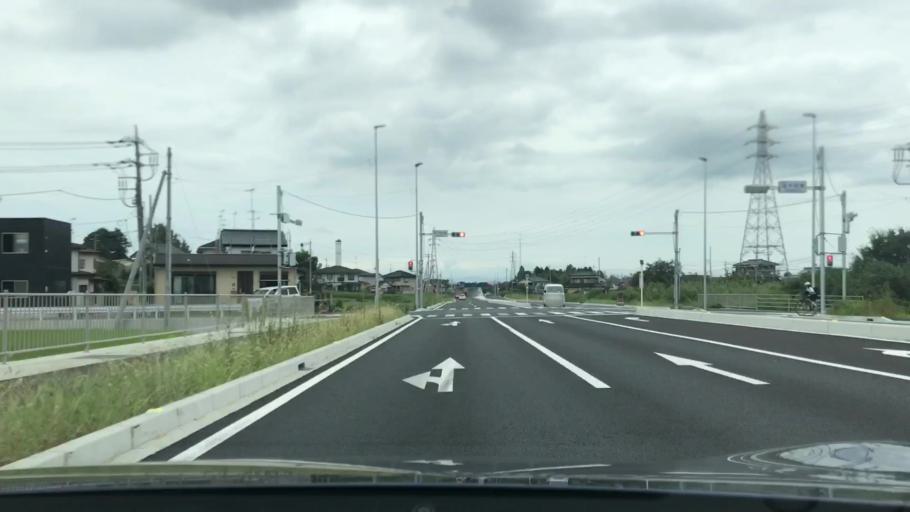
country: JP
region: Gunma
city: Tatebayashi
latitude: 36.2260
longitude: 139.5114
